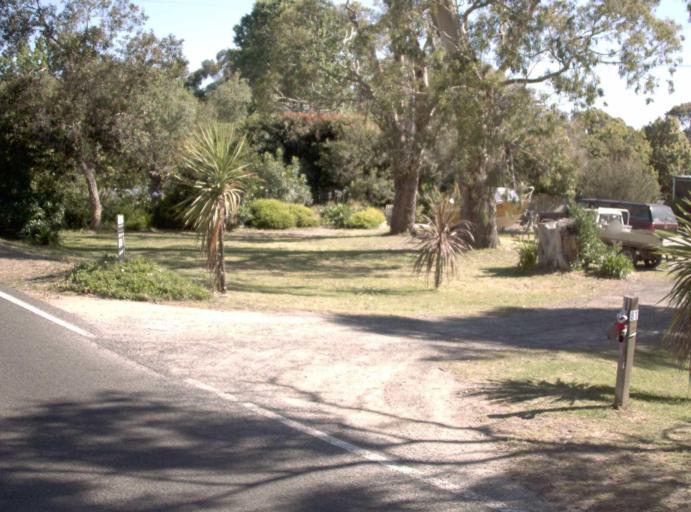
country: AU
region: Victoria
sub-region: Latrobe
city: Traralgon
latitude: -38.6535
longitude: 146.6767
